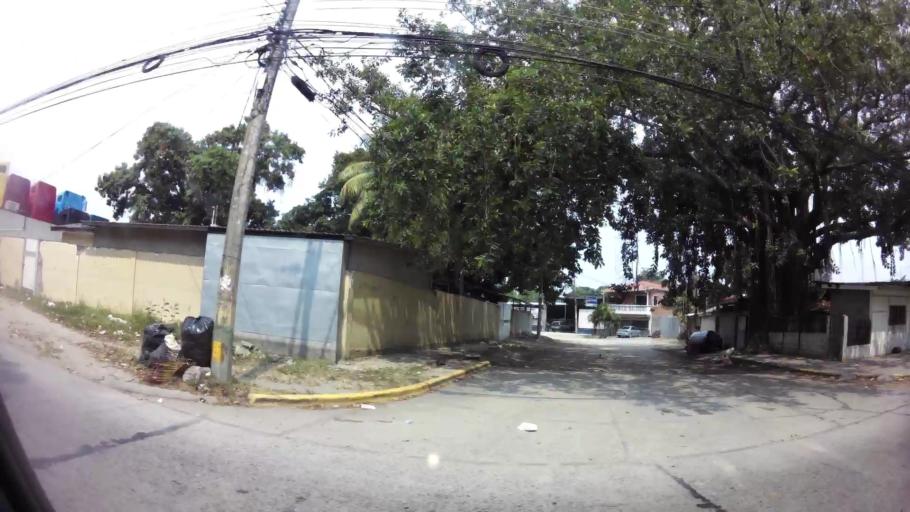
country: HN
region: Cortes
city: San Pedro Sula
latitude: 15.5086
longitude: -88.0127
